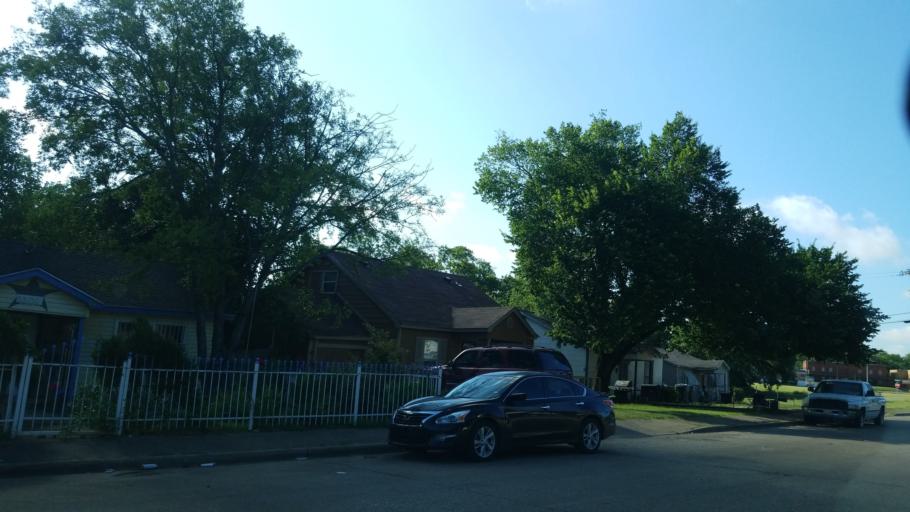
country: US
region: Texas
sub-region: Dallas County
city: Dallas
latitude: 32.7213
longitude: -96.8008
